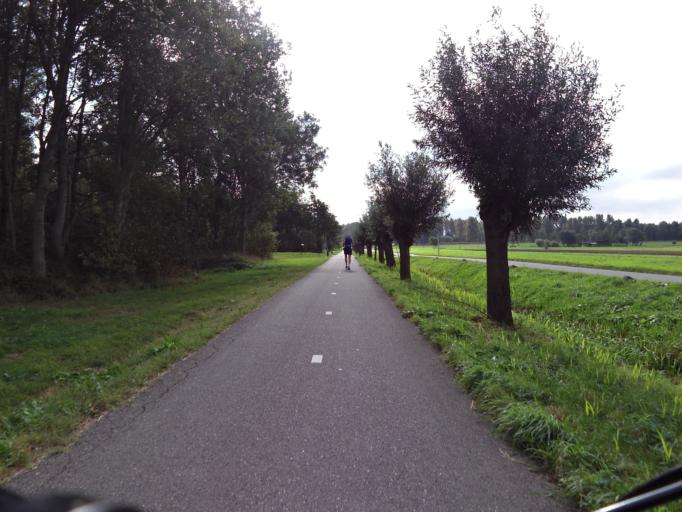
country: NL
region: South Holland
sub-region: Gemeente Zoetermeer
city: Zoetermeer
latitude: 52.0965
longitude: 4.5022
